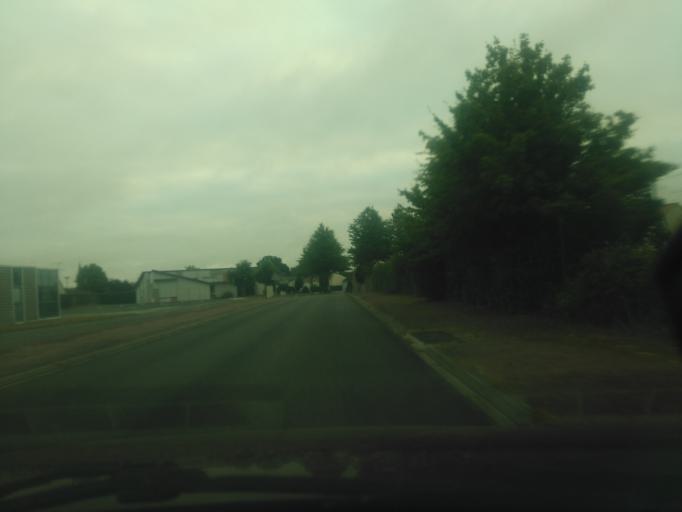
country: FR
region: Pays de la Loire
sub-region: Departement de la Vendee
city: La Ferriere
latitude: 46.7660
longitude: -1.3036
